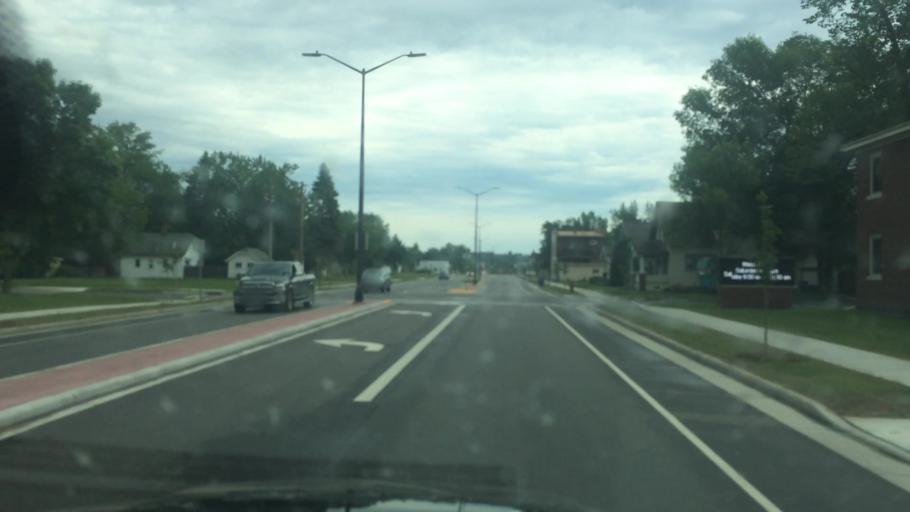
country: US
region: Wisconsin
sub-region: Marathon County
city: Wausau
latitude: 44.9483
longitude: -89.6472
